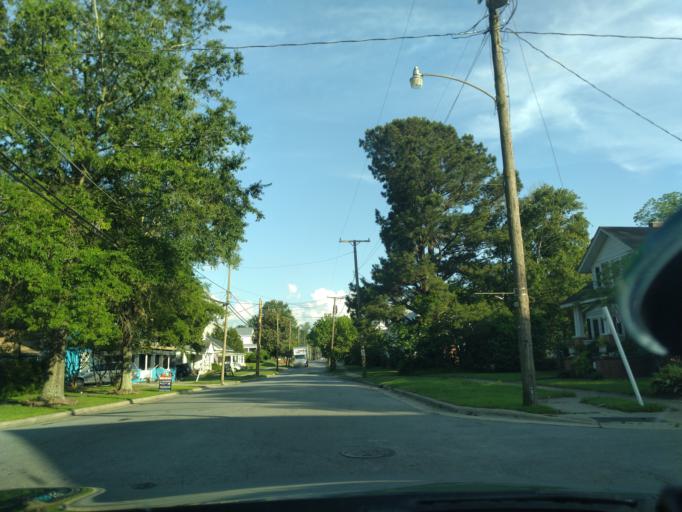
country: US
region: North Carolina
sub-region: Washington County
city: Plymouth
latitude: 35.8639
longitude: -76.7490
